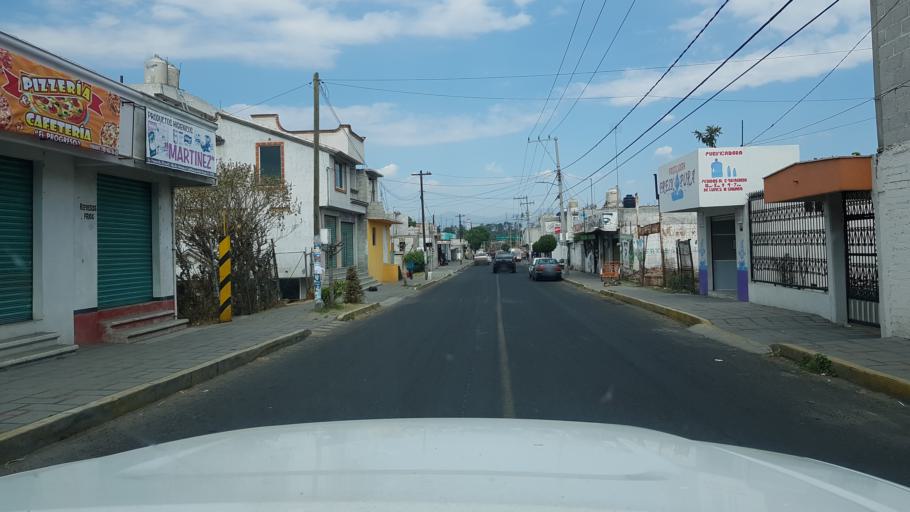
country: MX
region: Puebla
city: San Martin Texmelucan de Labastida
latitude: 19.2928
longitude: -98.4040
